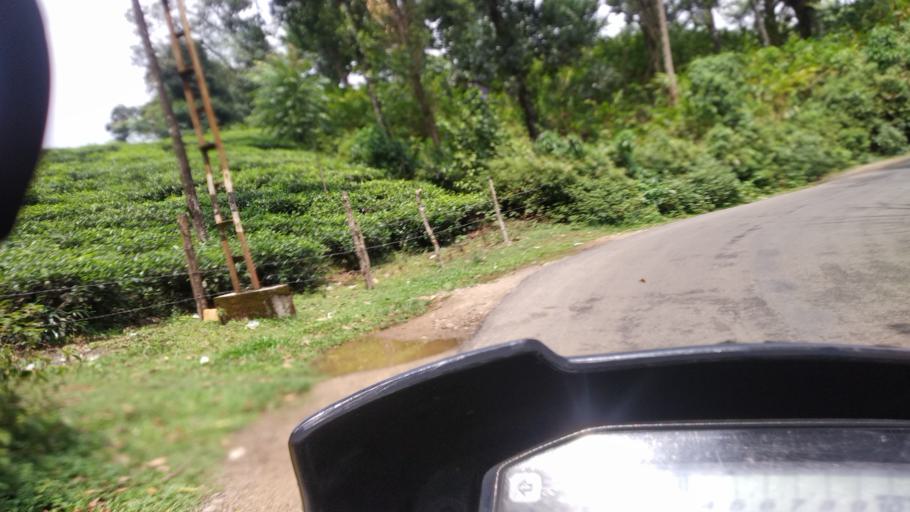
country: IN
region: Kerala
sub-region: Kottayam
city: Erattupetta
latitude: 9.6296
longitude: 76.9649
